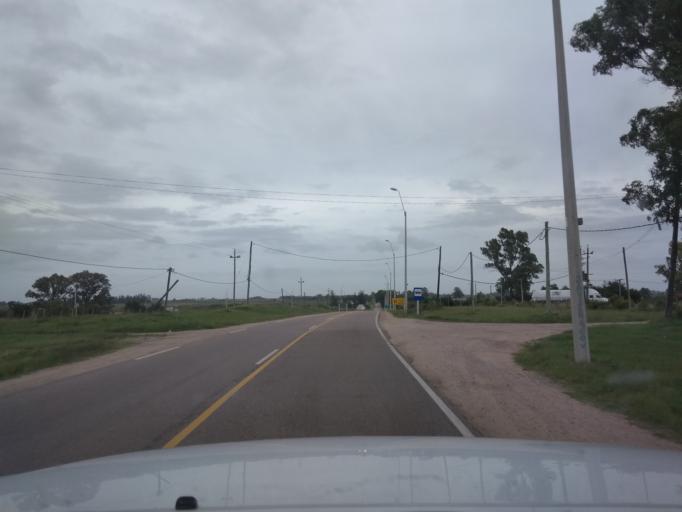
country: UY
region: Canelones
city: Tala
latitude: -34.3603
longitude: -55.7749
